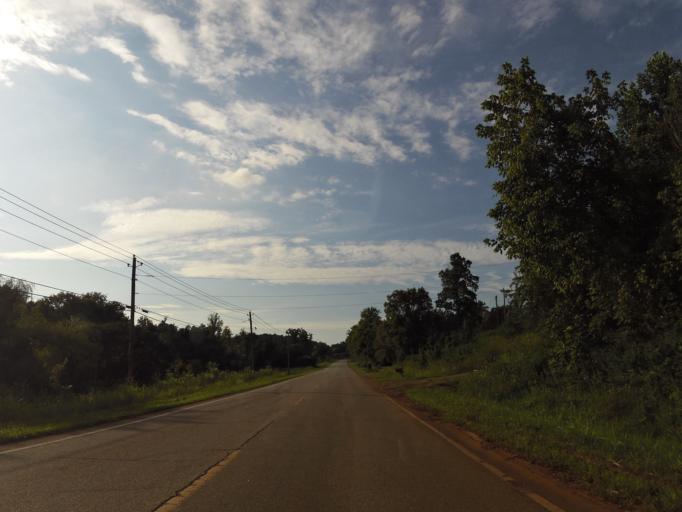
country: US
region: Tennessee
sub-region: Monroe County
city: Vonore
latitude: 35.6243
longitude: -84.3102
